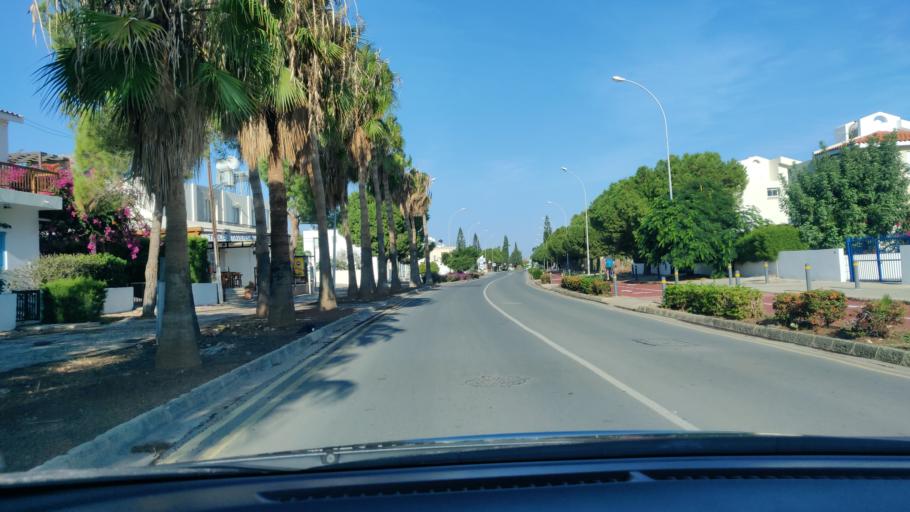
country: CY
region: Ammochostos
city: Protaras
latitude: 35.0118
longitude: 34.0523
